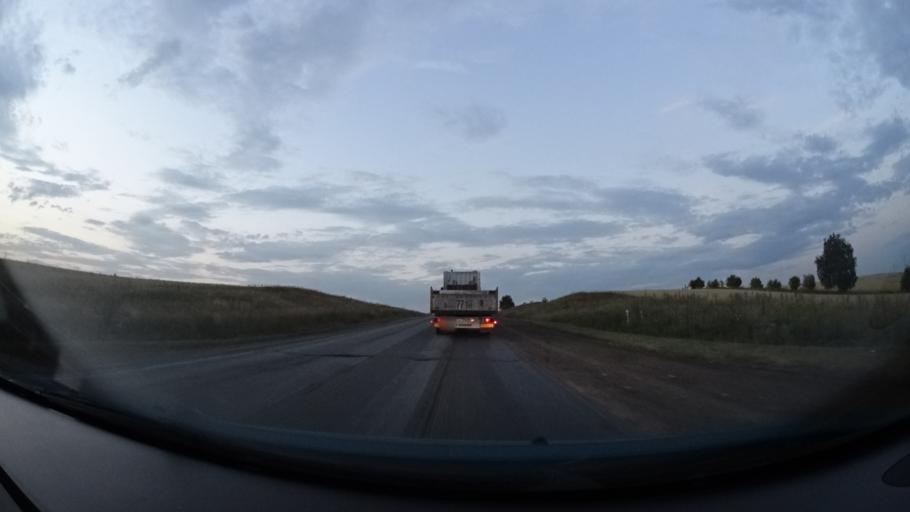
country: RU
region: Tatarstan
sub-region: Bavlinskiy Rayon
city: Bavly
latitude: 54.2950
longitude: 53.0061
